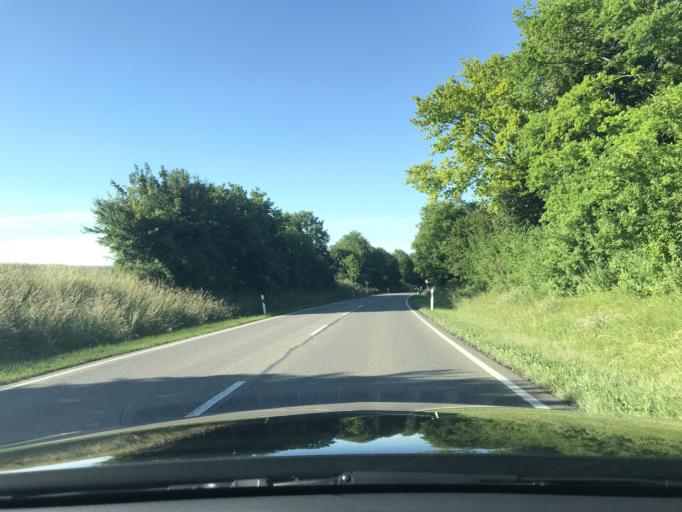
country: DE
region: Baden-Wuerttemberg
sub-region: Regierungsbezirk Stuttgart
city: Stuttgart Muehlhausen
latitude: 48.8442
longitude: 9.2517
